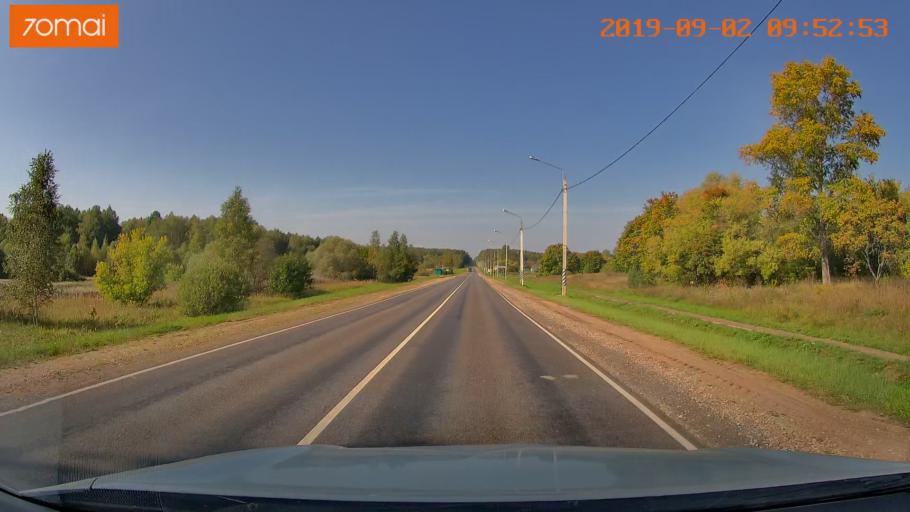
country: RU
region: Kaluga
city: Mosal'sk
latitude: 54.5857
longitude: 34.6910
